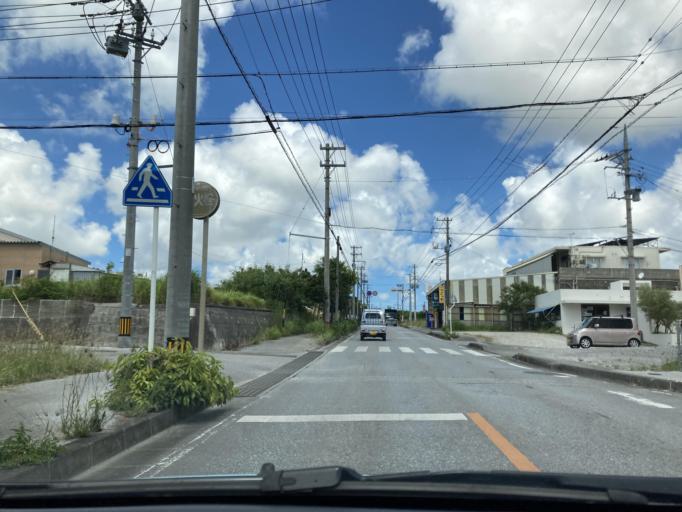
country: JP
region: Okinawa
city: Tomigusuku
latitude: 26.1457
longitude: 127.7259
